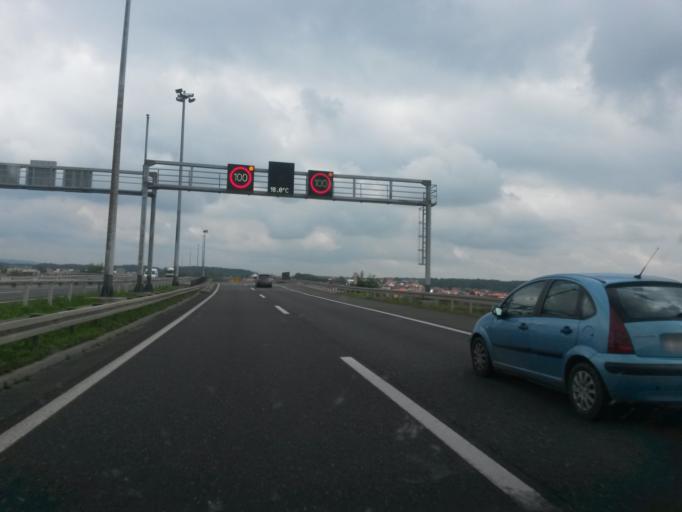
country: HR
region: Grad Zagreb
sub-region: Sesvete
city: Sesvete
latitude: 45.8171
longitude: 16.1380
